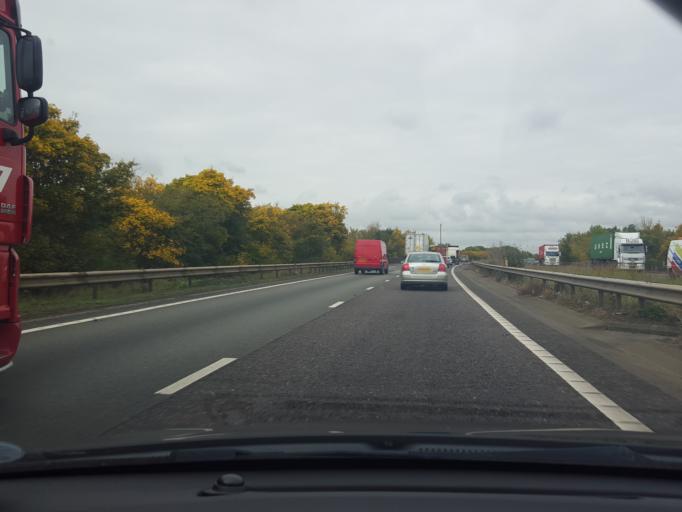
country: GB
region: England
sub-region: Suffolk
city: Bramford
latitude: 52.1017
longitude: 1.1084
